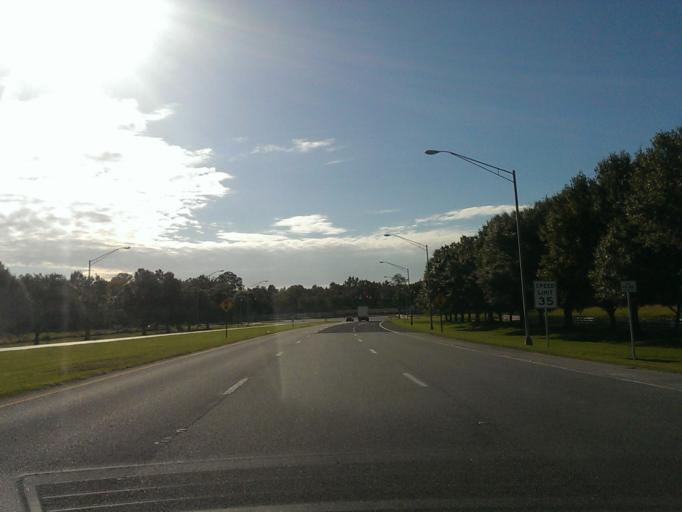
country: US
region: Florida
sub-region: Osceola County
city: Celebration
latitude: 28.3030
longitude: -81.5672
